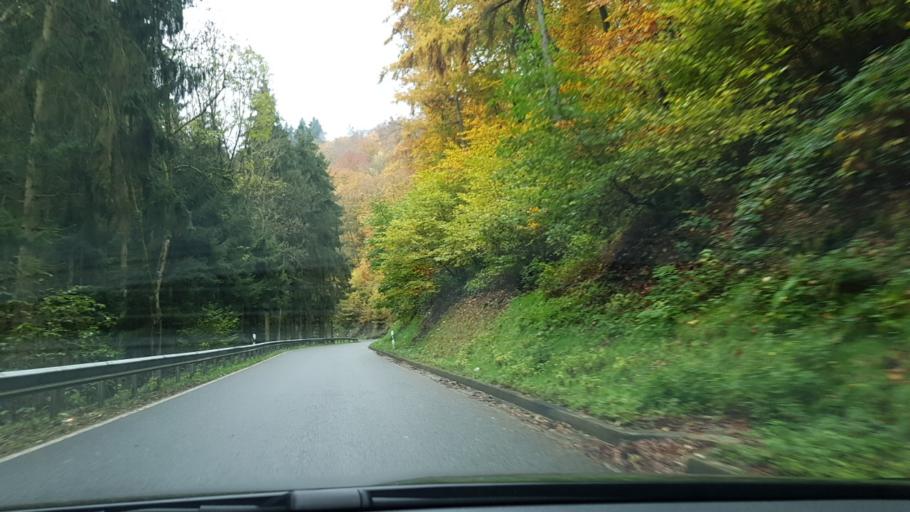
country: DE
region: Rheinland-Pfalz
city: Mehring
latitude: 49.7839
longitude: 6.8381
